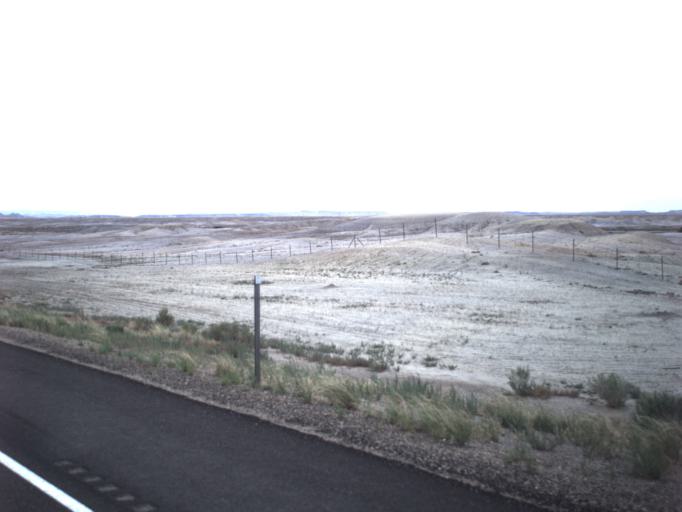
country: US
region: Utah
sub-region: Carbon County
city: East Carbon City
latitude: 38.9876
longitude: -110.2431
